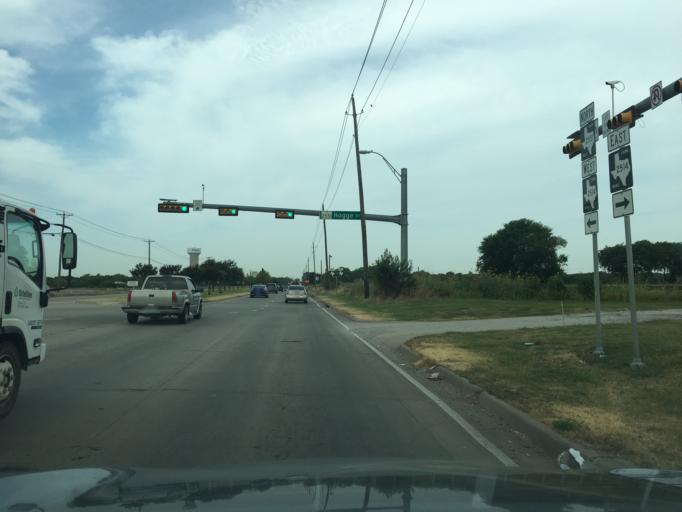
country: US
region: Texas
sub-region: Collin County
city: Parker
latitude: 33.0554
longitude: -96.6116
